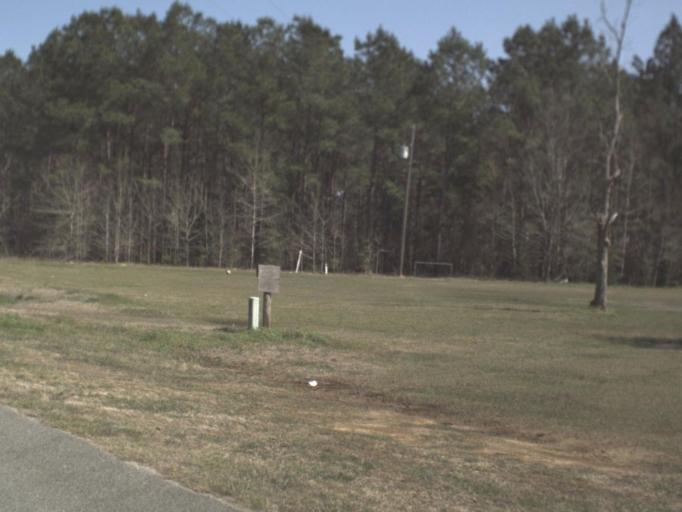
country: US
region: Florida
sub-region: Gadsden County
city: Gretna
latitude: 30.5725
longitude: -84.7050
